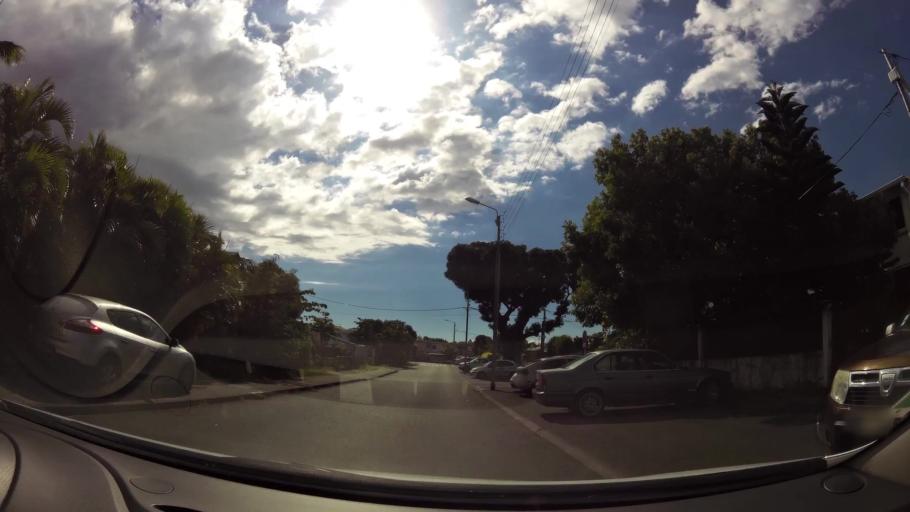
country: RE
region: Reunion
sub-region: Reunion
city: Saint-Denis
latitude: -20.8898
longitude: 55.4846
